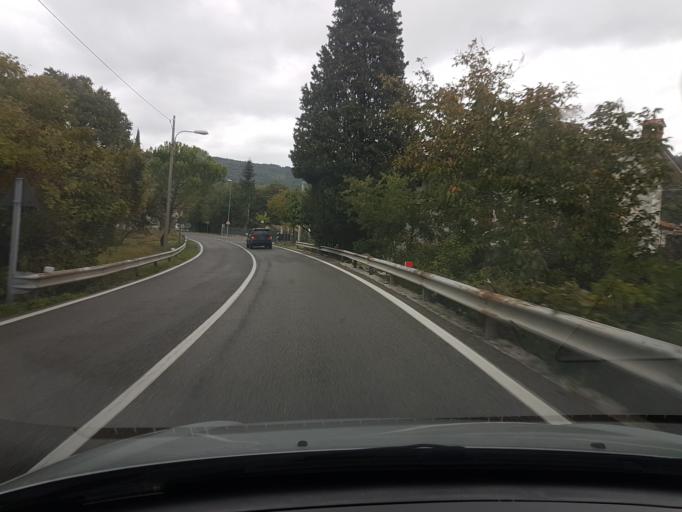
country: IT
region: Friuli Venezia Giulia
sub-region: Provincia di Gorizia
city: Monfalcone
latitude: 45.8194
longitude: 13.5798
